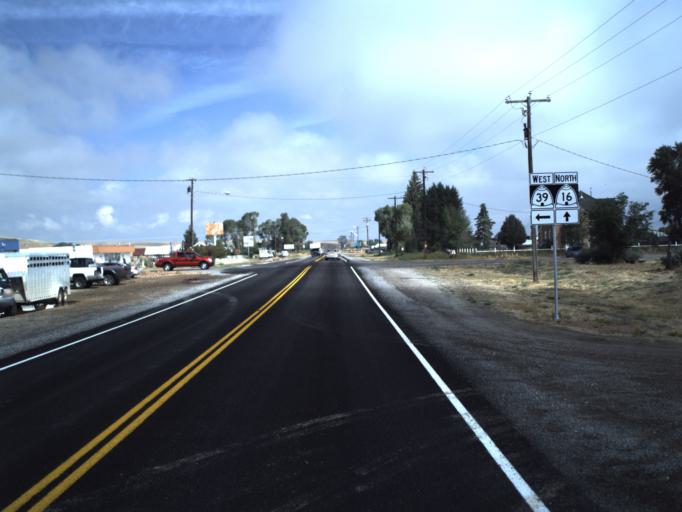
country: US
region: Utah
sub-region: Rich County
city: Randolph
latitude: 41.5232
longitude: -111.1629
